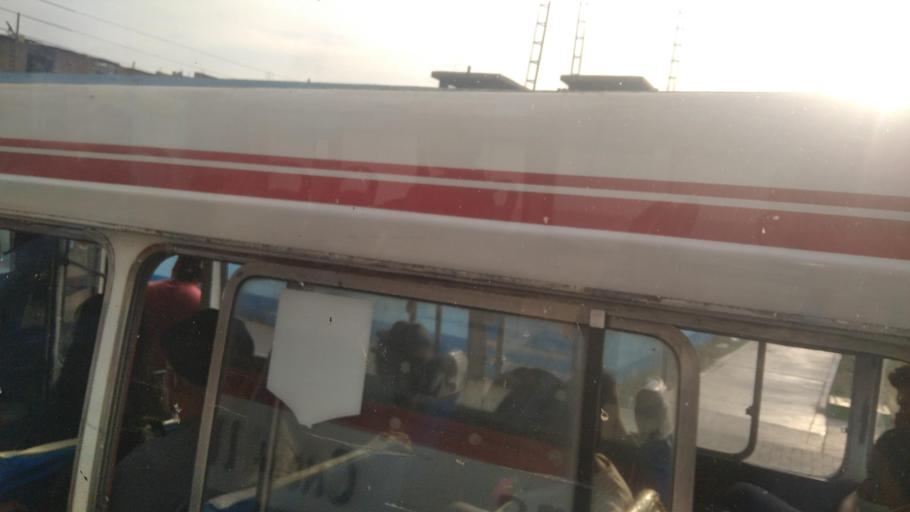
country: PE
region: Lima
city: Lima
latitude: -12.0199
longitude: -77.0014
